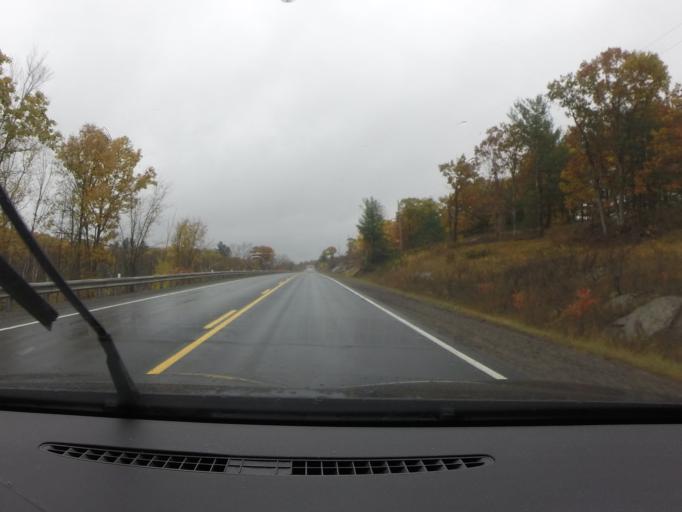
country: CA
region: Ontario
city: Greater Napanee
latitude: 44.6346
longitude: -77.1381
